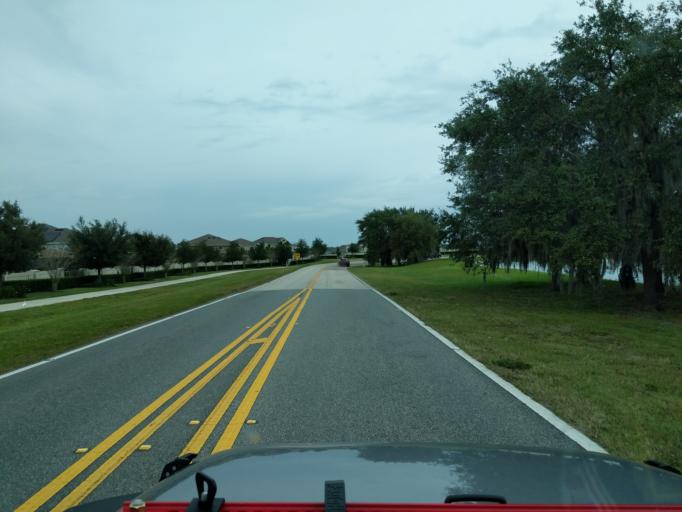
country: US
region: Florida
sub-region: Orange County
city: Oakland
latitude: 28.5238
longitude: -81.6203
